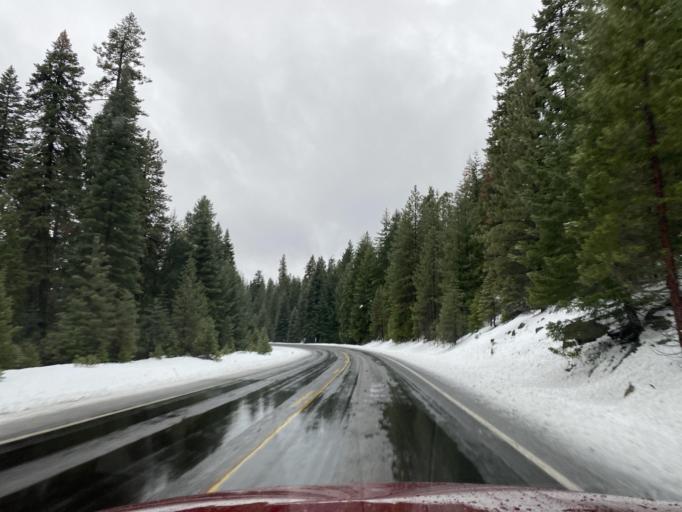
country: US
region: Oregon
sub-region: Klamath County
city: Klamath Falls
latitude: 42.4964
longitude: -122.0850
